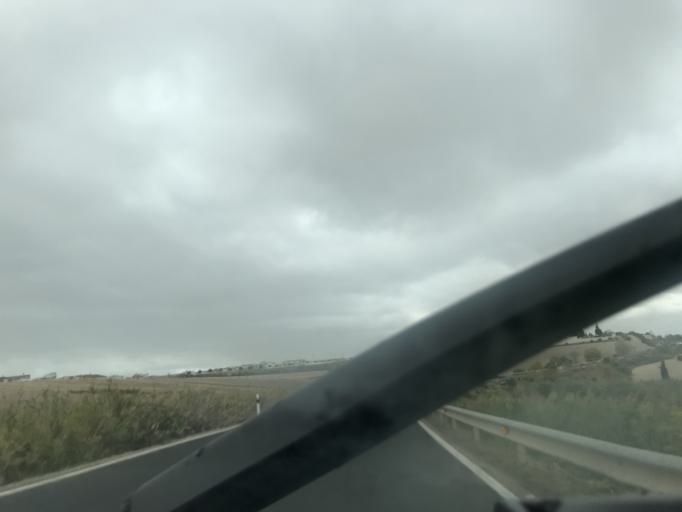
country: ES
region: Andalusia
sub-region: Provincia de Jaen
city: Peal de Becerro
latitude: 37.9174
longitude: -3.1136
